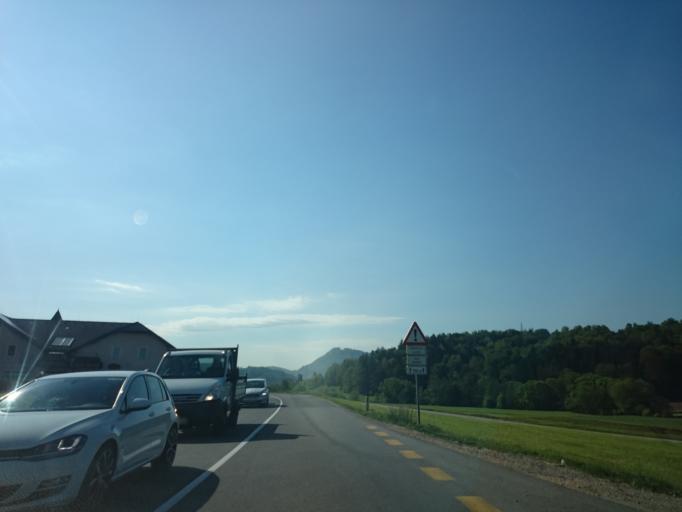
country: SI
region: Sentjur pri Celju
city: Sentjur
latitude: 46.2333
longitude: 15.3854
